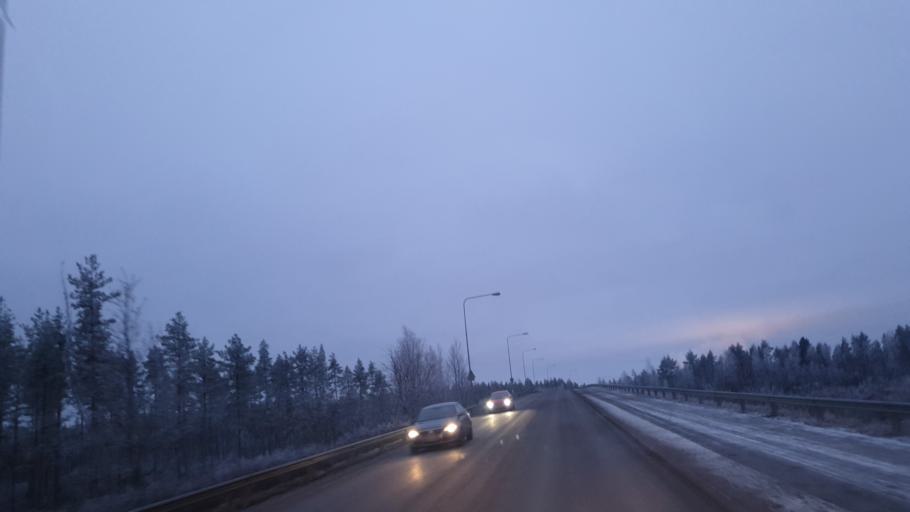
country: FI
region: Southern Ostrobothnia
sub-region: Seinaejoki
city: Nurmo
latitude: 62.7757
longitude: 22.8909
